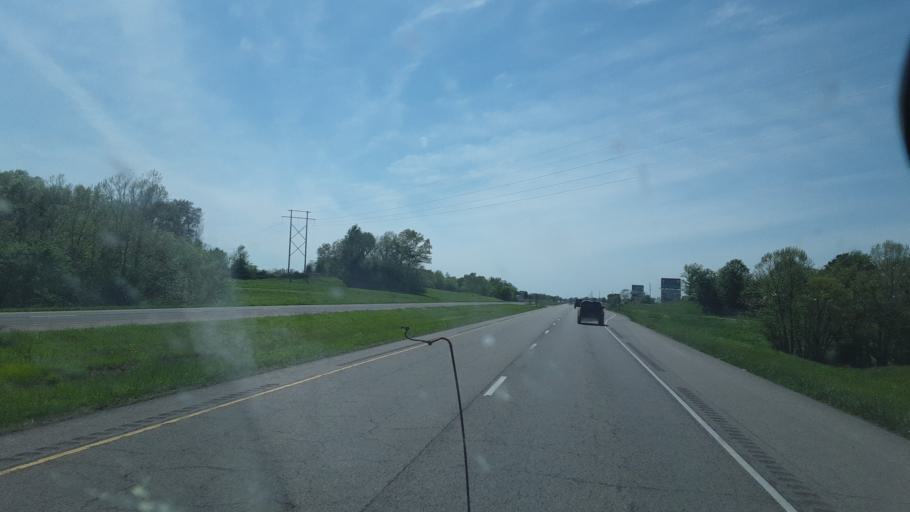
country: US
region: Illinois
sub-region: Williamson County
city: Marion
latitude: 37.7298
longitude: -88.8252
